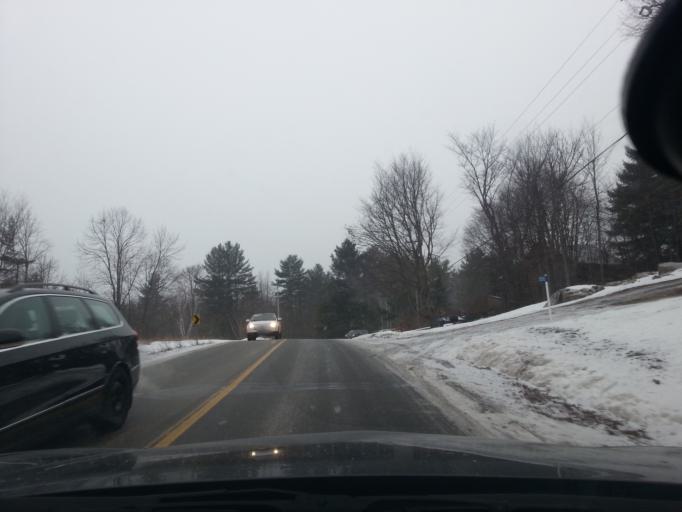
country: CA
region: Ontario
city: Arnprior
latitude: 45.3223
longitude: -76.3246
